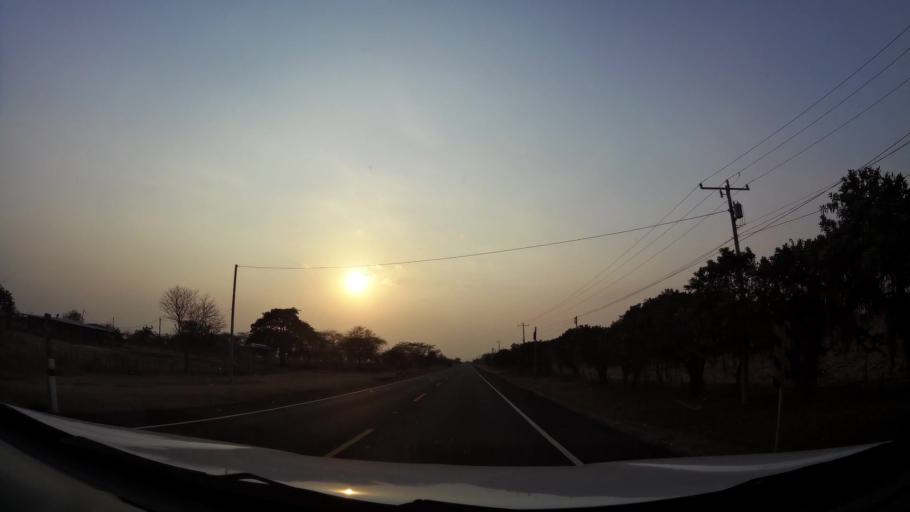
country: NI
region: Leon
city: La Paz Centro
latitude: 12.3221
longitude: -86.6198
